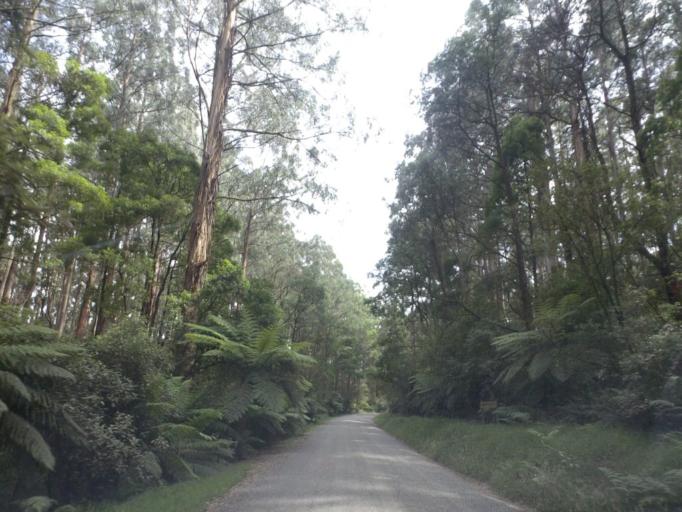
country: AU
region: Victoria
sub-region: Yarra Ranges
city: Healesville
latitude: -37.5333
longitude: 145.5156
